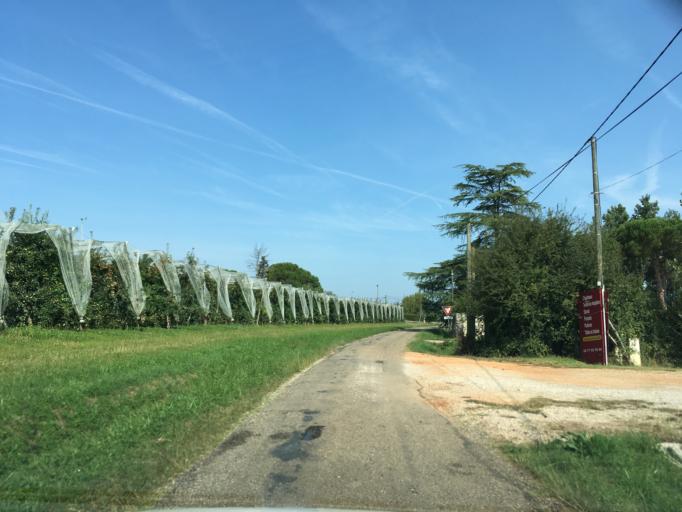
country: FR
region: Midi-Pyrenees
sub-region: Departement du Tarn-et-Garonne
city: Albias
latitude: 44.0655
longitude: 1.4184
